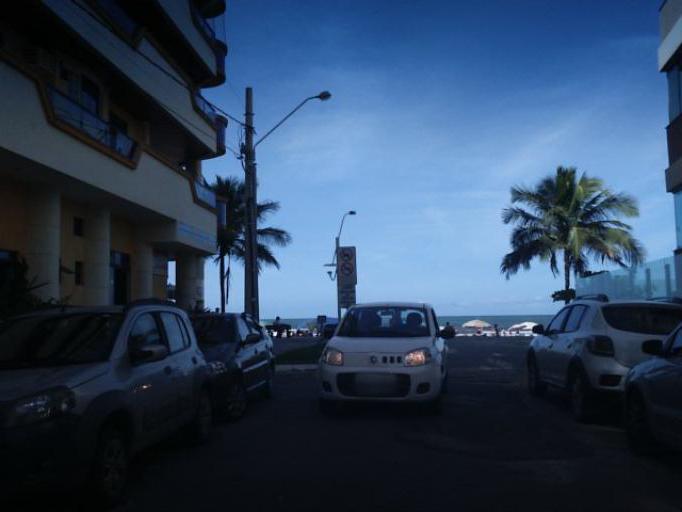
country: BR
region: Santa Catarina
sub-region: Itapema
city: Itapema
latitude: -27.1202
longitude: -48.6065
